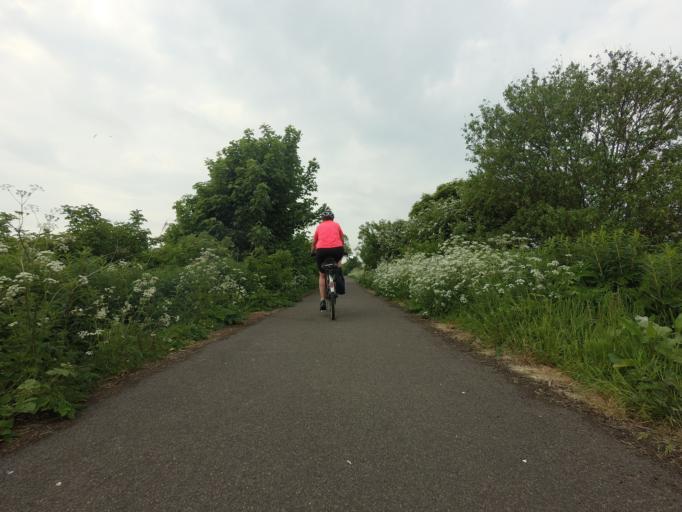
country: GB
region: Scotland
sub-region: Fife
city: Townhill
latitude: 56.0880
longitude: -3.4431
